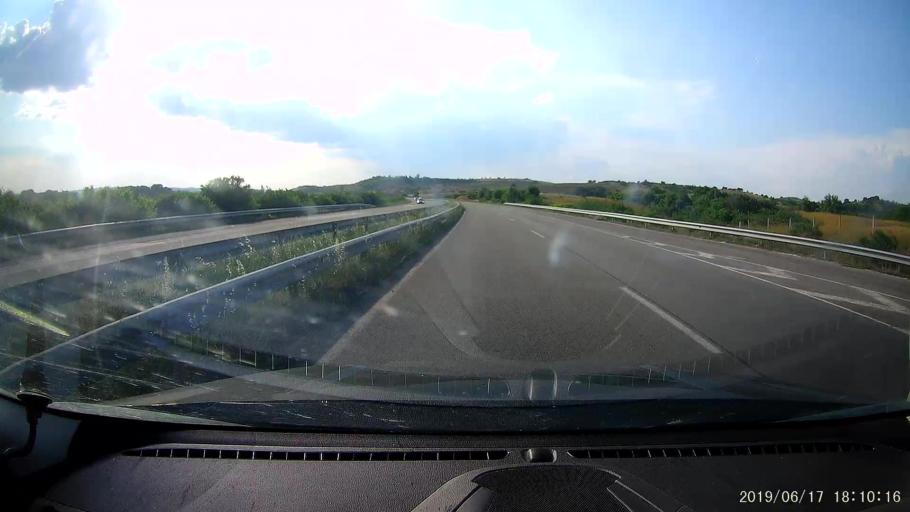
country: BG
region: Khaskovo
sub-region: Obshtina Lyubimets
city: Lyubimets
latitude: 41.8725
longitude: 26.0807
